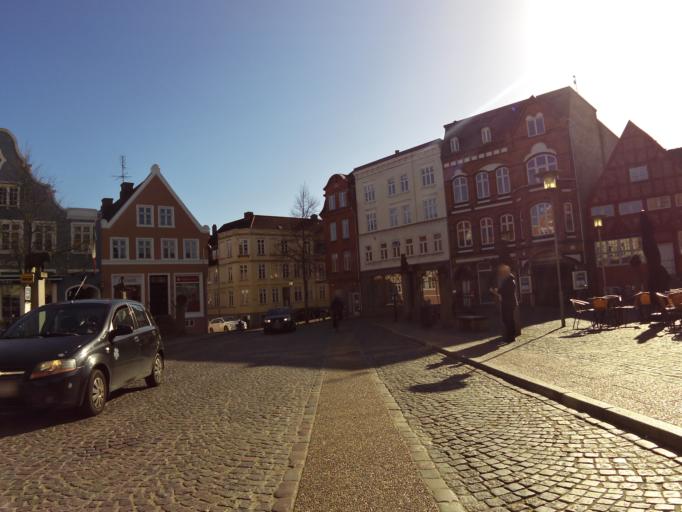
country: DK
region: South Denmark
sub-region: Haderslev Kommune
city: Haderslev
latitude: 55.2492
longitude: 9.4881
